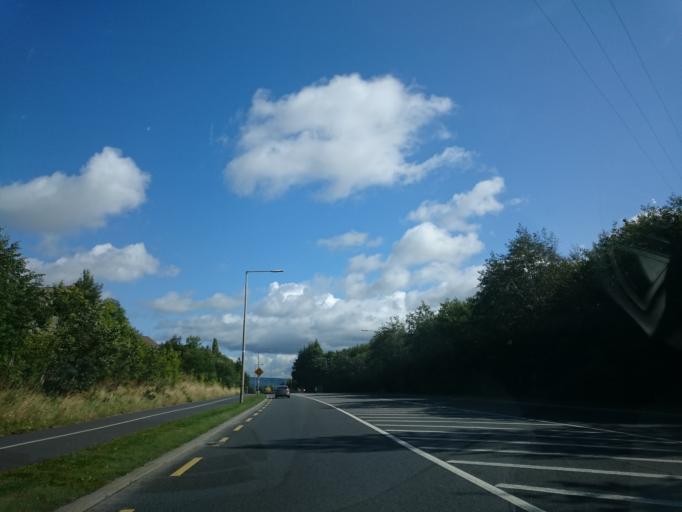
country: IE
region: Leinster
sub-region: Kilkenny
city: Kilkenny
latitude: 52.6393
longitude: -7.2341
